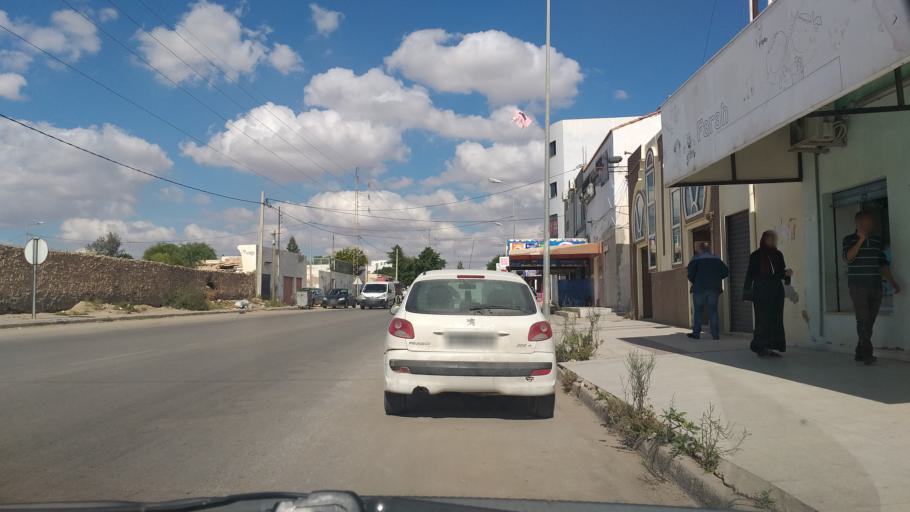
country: TN
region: Safaqis
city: Al Qarmadah
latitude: 34.7702
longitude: 10.7746
